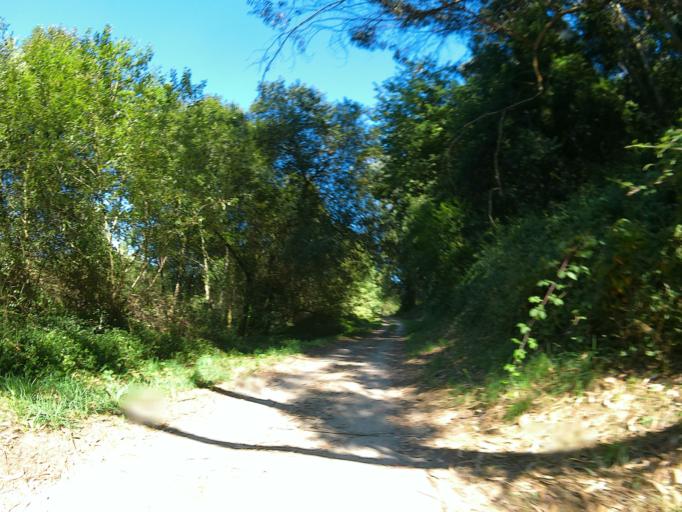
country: PT
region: Viana do Castelo
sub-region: Ponte de Lima
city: Ponte de Lima
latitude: 41.7620
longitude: -8.6065
